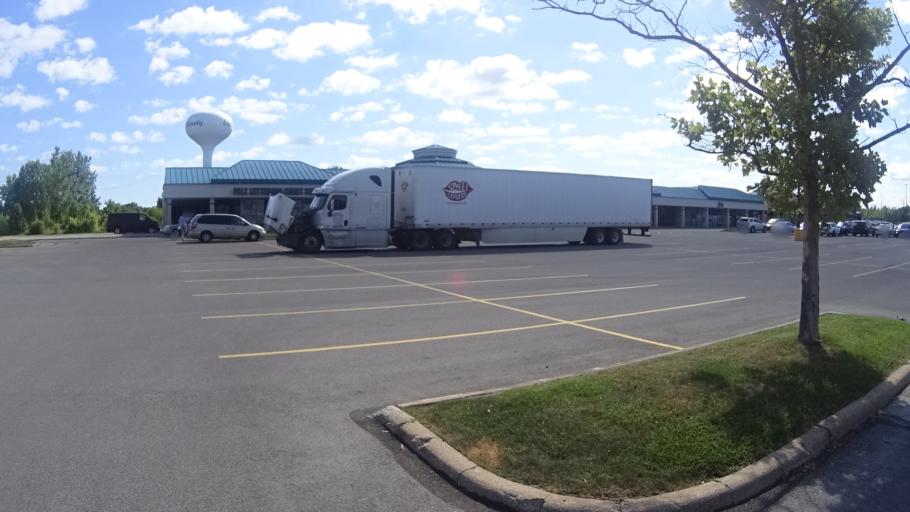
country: US
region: Ohio
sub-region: Erie County
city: Sandusky
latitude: 41.4054
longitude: -82.6584
